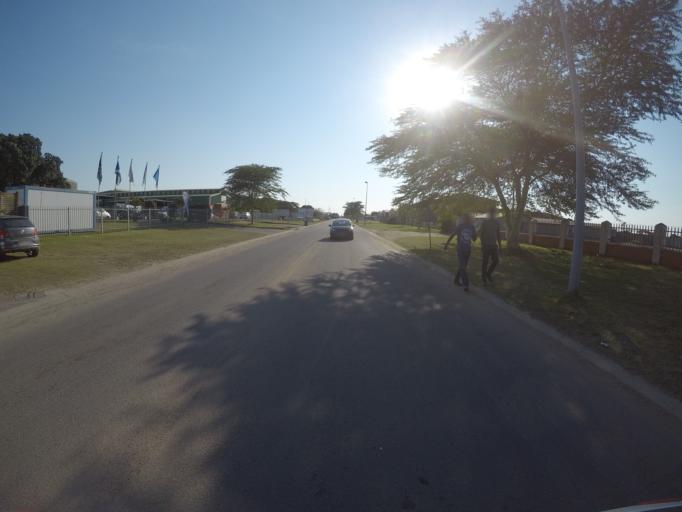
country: ZA
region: KwaZulu-Natal
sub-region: uThungulu District Municipality
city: Richards Bay
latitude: -28.7434
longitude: 32.0364
